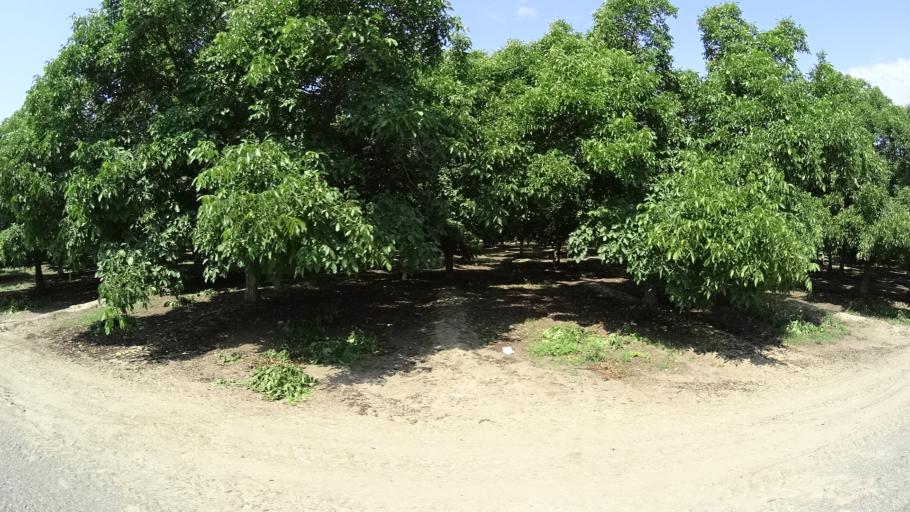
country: US
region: California
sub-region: Fresno County
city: Laton
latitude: 36.3978
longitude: -119.7450
